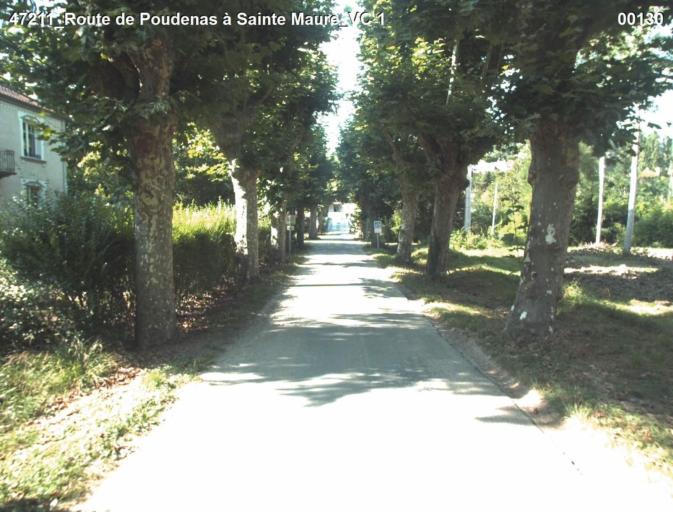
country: FR
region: Aquitaine
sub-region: Departement du Lot-et-Garonne
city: Mezin
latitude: 44.0440
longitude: 0.2104
